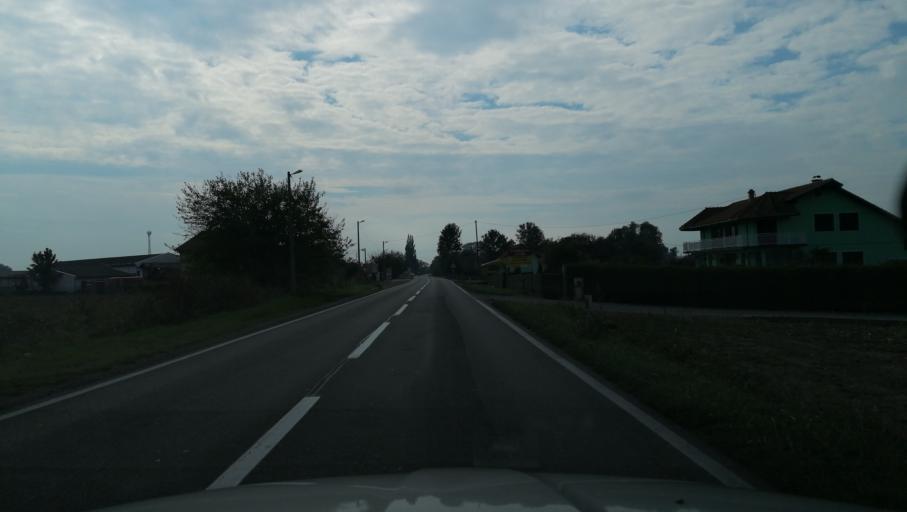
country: BA
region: Republika Srpska
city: Dvorovi
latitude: 44.8223
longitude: 19.2796
